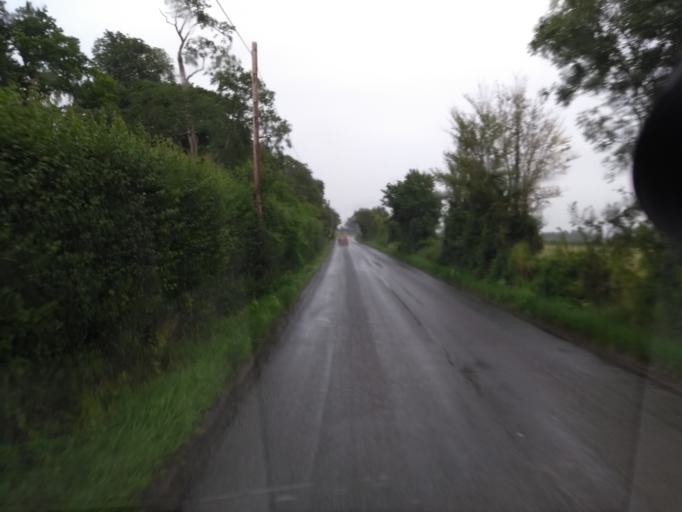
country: GB
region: England
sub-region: Somerset
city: Ilchester
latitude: 51.0758
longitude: -2.6865
